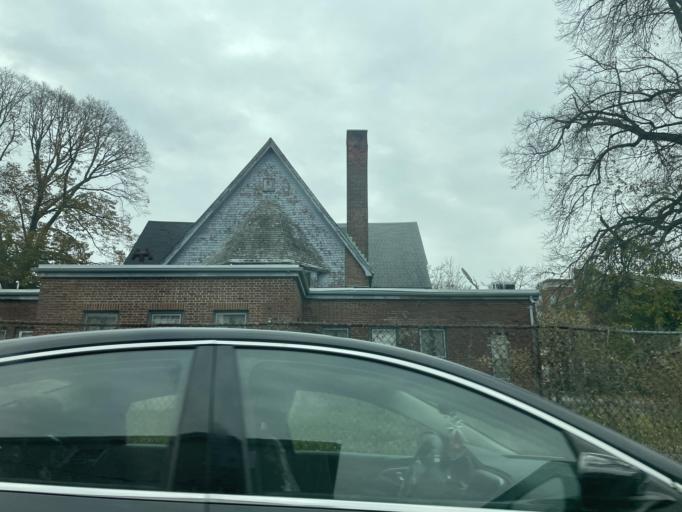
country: US
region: Massachusetts
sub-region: Bristol County
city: Fall River
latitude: 41.6926
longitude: -71.1343
